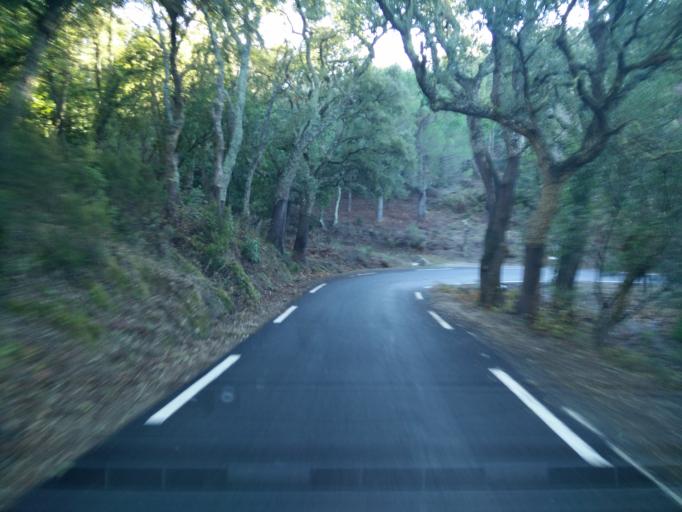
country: FR
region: Provence-Alpes-Cote d'Azur
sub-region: Departement du Var
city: Collobrieres
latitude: 43.2389
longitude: 6.3552
